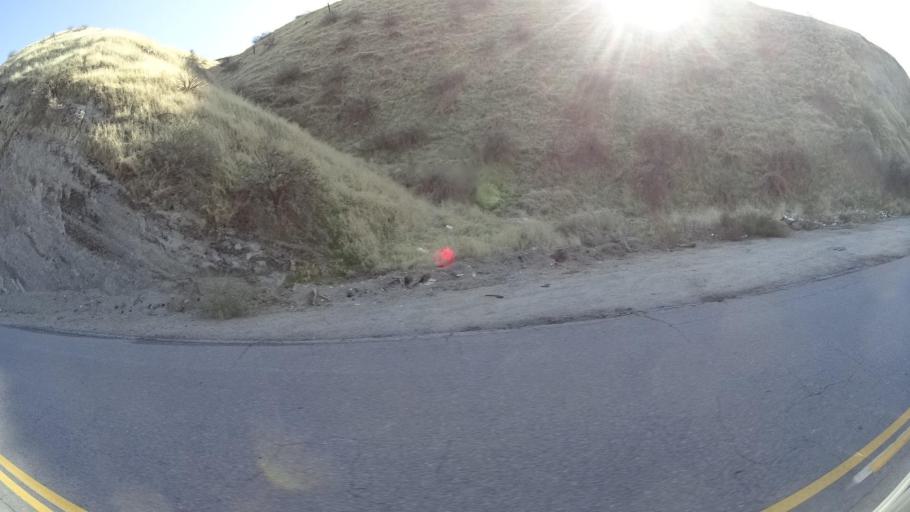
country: US
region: California
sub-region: Kern County
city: Arvin
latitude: 35.3237
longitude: -118.7169
